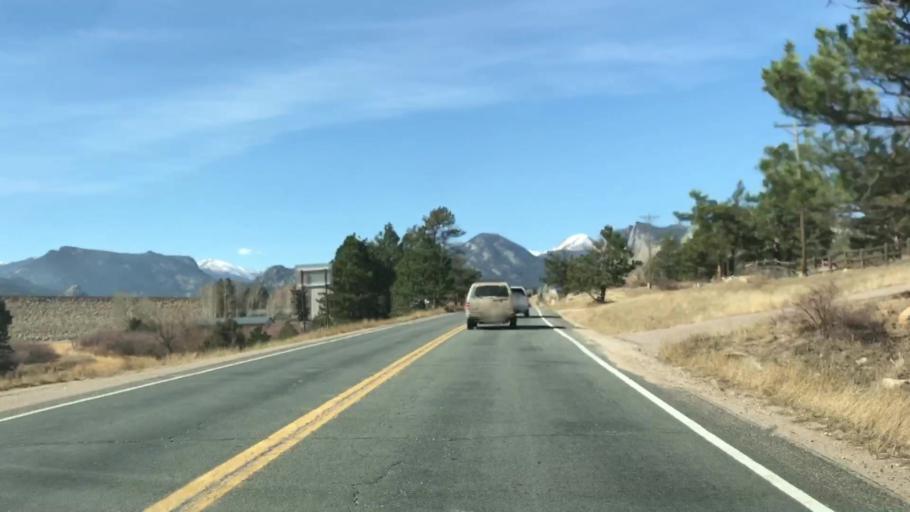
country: US
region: Colorado
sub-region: Larimer County
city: Estes Park
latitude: 40.3768
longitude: -105.4849
